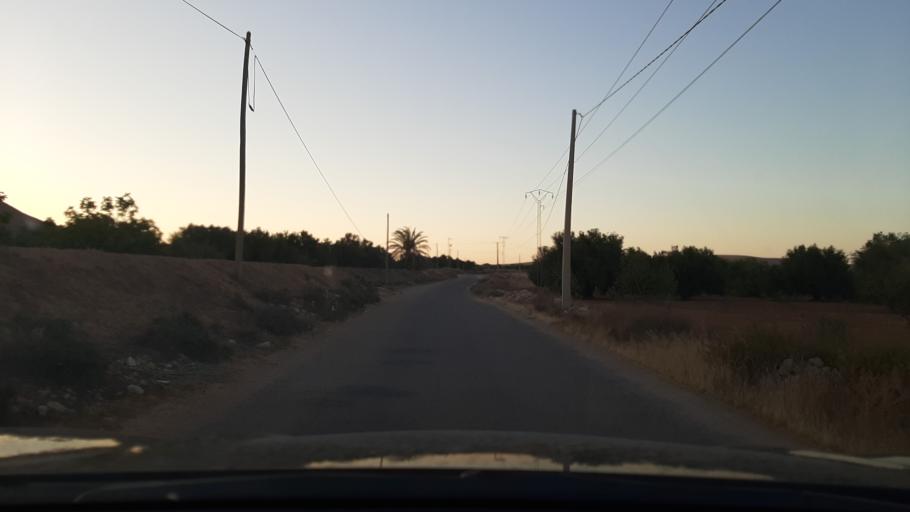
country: TN
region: Qabis
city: Matmata
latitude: 33.5521
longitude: 10.1873
